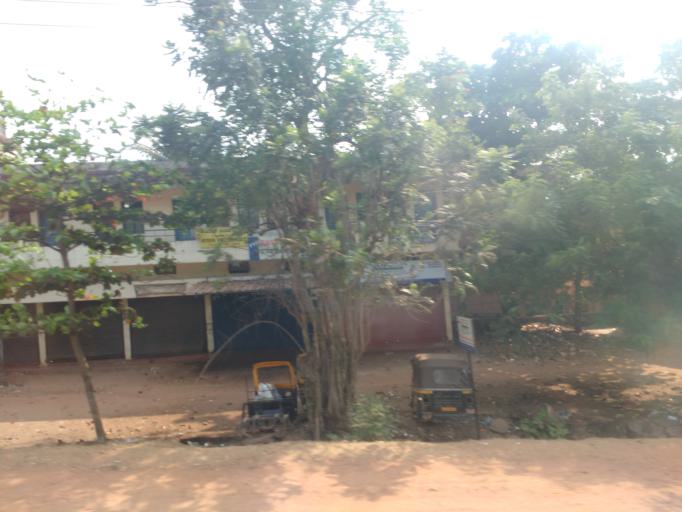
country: IN
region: Karnataka
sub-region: Dakshina Kannada
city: Mangalore
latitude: 12.8694
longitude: 74.8707
